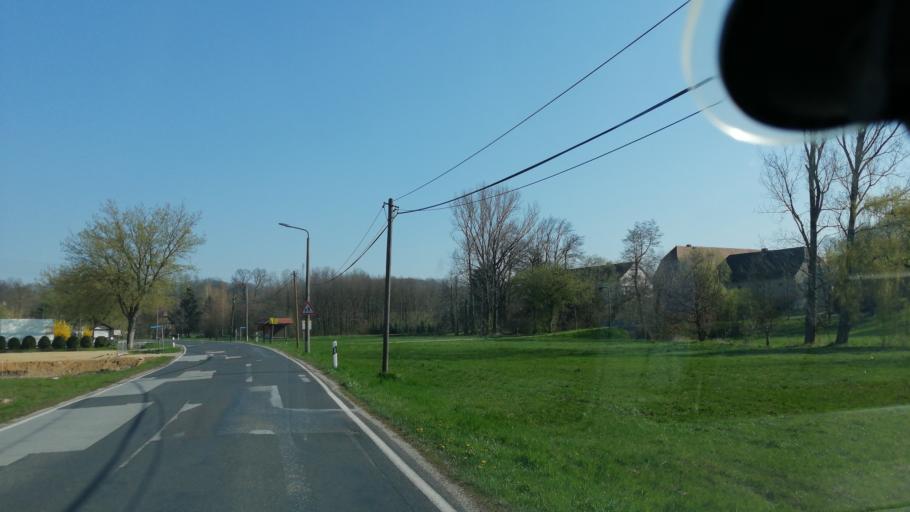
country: DE
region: Saxony
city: Goerlitz
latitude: 51.1739
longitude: 14.9350
